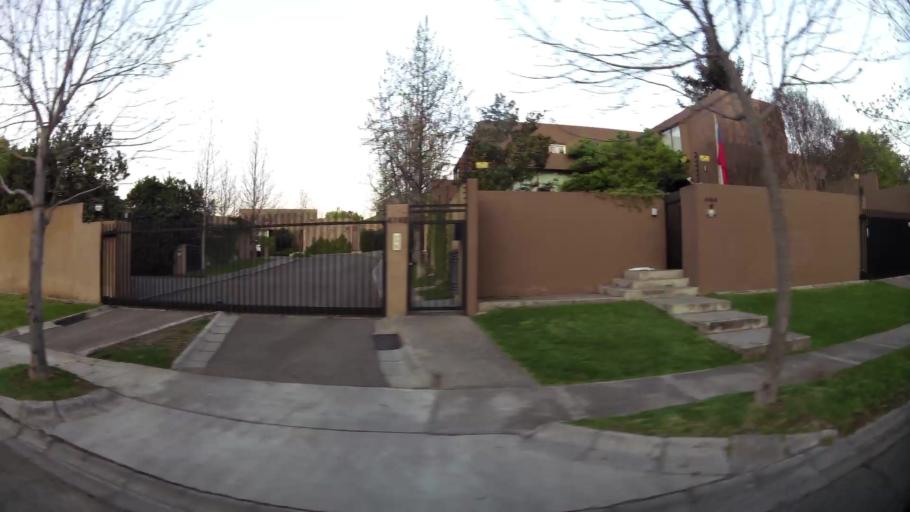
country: CL
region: Santiago Metropolitan
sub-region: Provincia de Chacabuco
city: Chicureo Abajo
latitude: -33.3395
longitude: -70.5514
